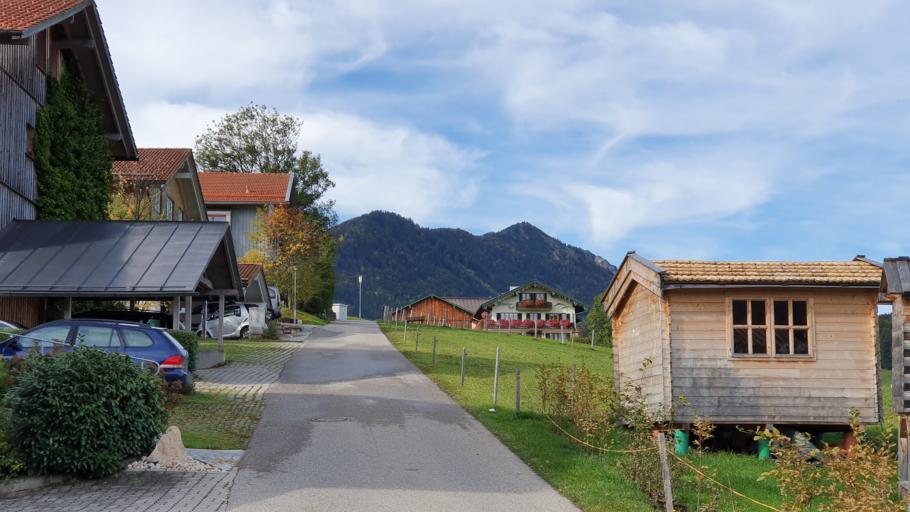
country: DE
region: Bavaria
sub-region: Upper Bavaria
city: Ruhpolding
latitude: 47.7578
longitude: 12.6415
